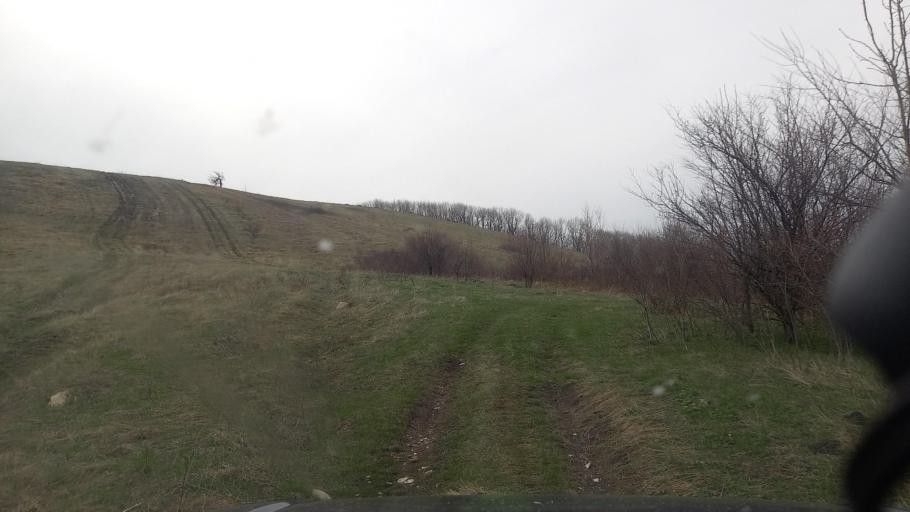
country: RU
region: Krasnodarskiy
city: Divnomorskoye
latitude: 44.6159
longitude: 38.2170
